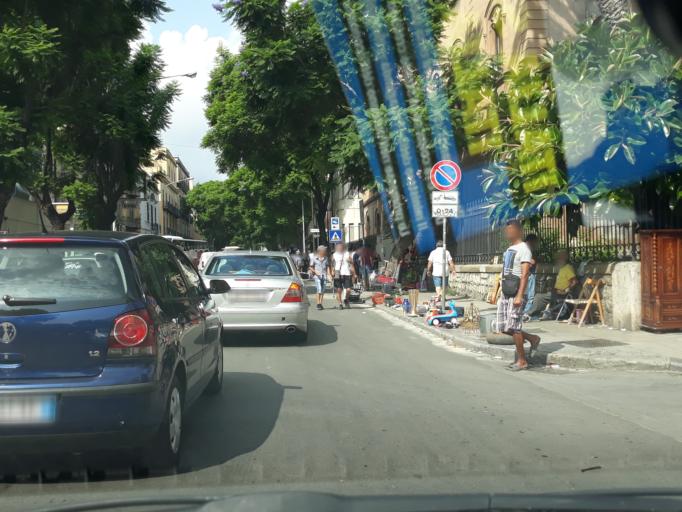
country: IT
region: Sicily
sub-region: Palermo
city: Palermo
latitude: 38.1091
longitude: 13.3605
